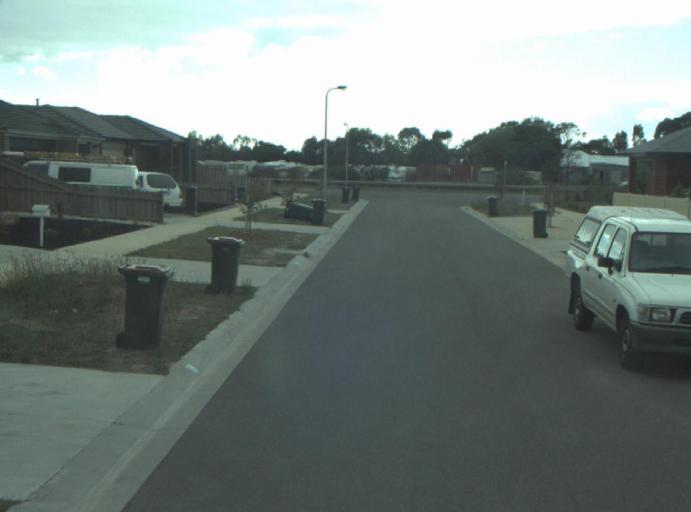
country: AU
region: Victoria
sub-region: Greater Geelong
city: Breakwater
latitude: -38.2052
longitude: 144.3499
